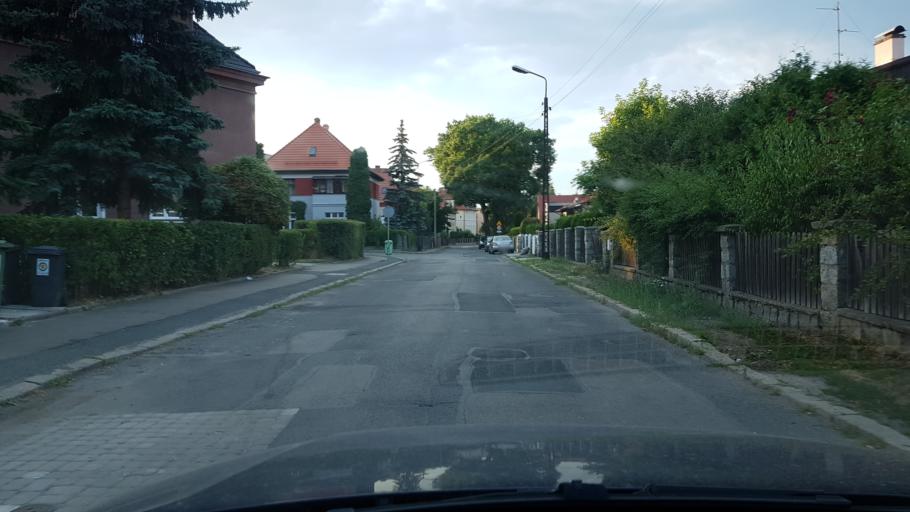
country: PL
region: Lower Silesian Voivodeship
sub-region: Jelenia Gora
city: Jelenia Gora
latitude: 50.8918
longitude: 15.7321
